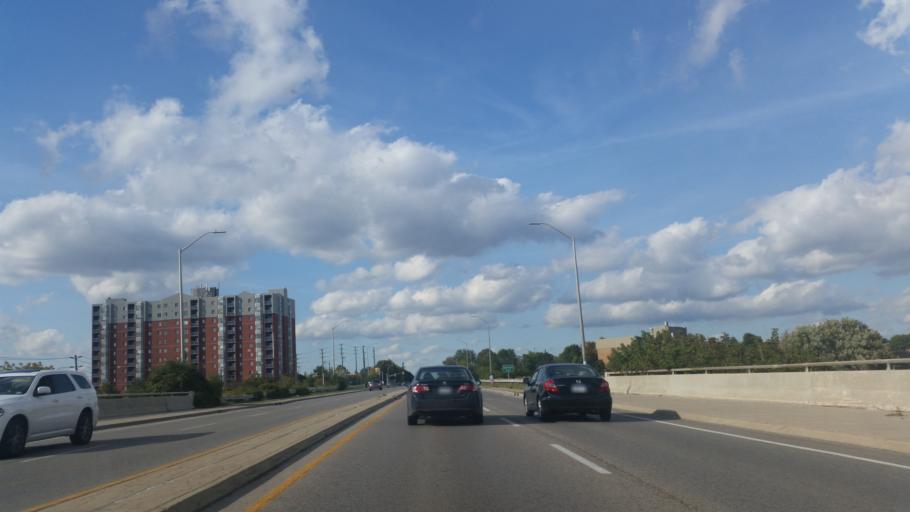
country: CA
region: Ontario
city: London
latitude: 42.9920
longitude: -81.2968
